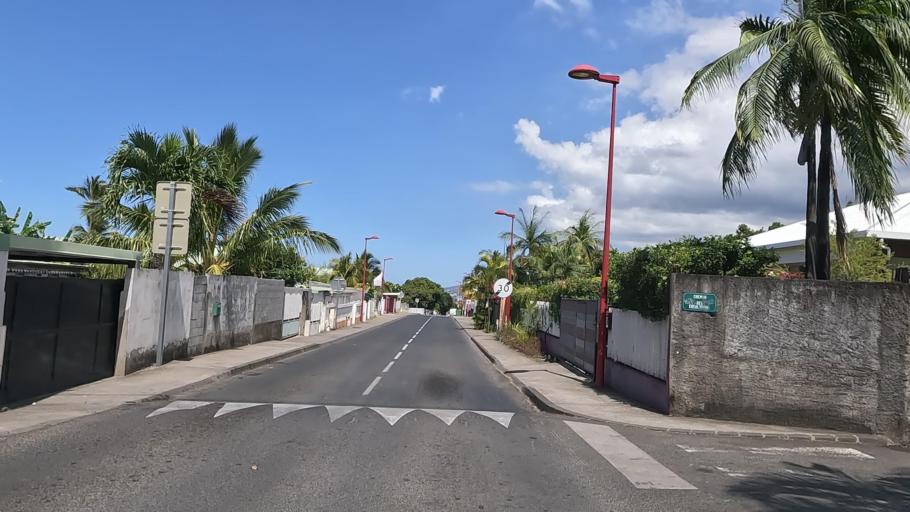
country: RE
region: Reunion
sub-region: Reunion
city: Saint-Louis
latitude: -21.2779
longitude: 55.4475
